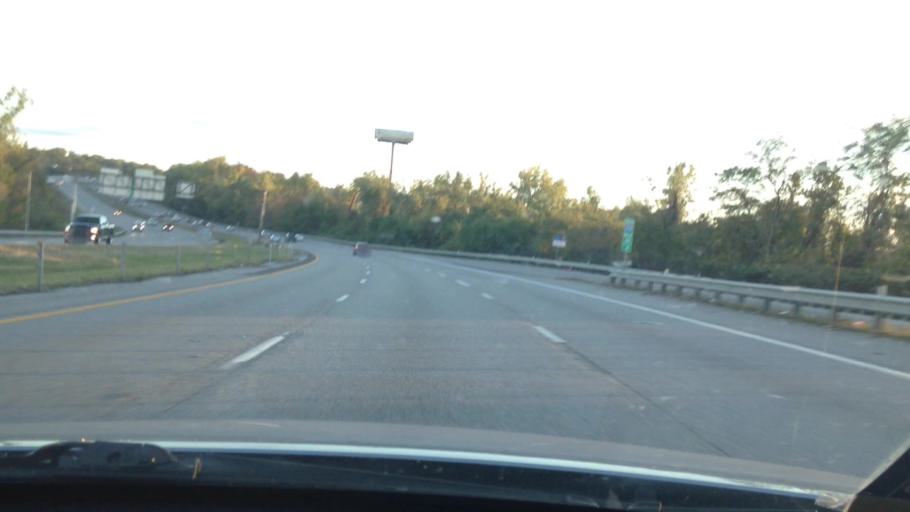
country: US
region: Missouri
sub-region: Jackson County
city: Sugar Creek
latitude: 39.0810
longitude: -94.4911
